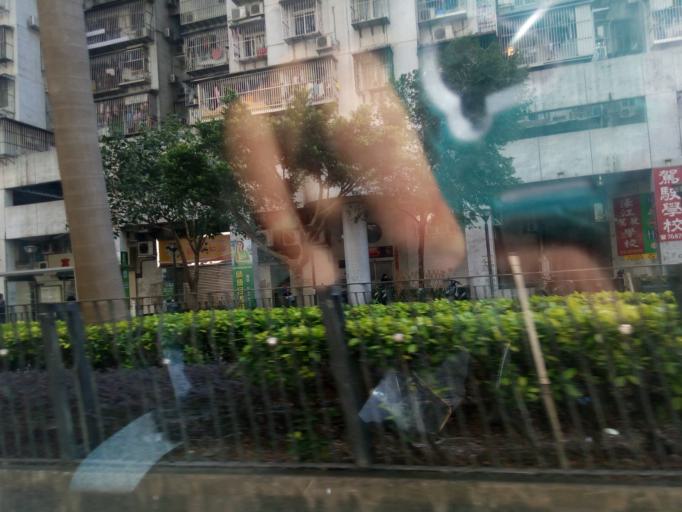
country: MO
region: Macau
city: Macau
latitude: 22.2060
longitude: 113.5546
